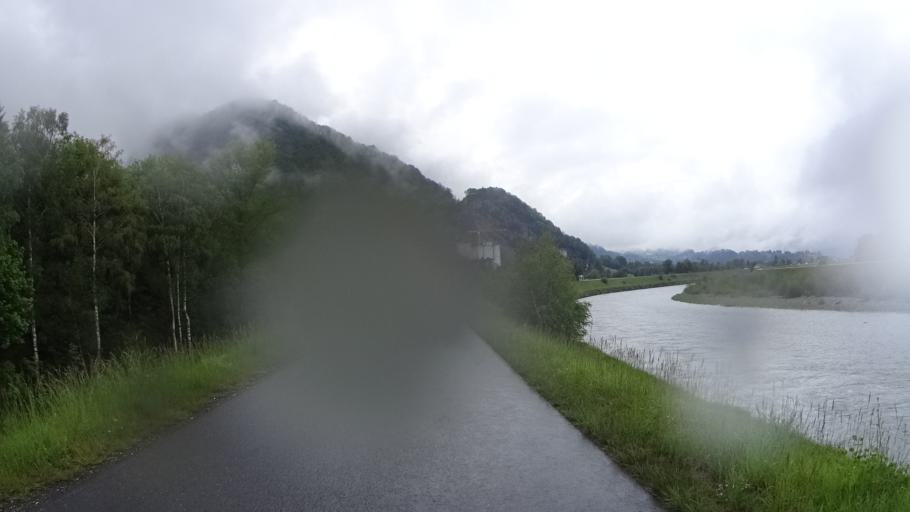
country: LI
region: Balzers
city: Balzers
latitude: 47.0613
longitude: 9.4709
